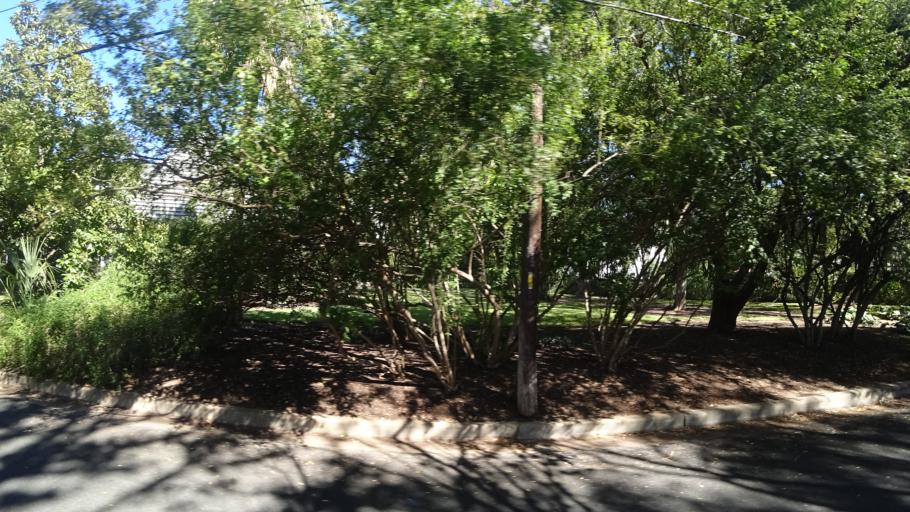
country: US
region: Texas
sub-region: Travis County
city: Rollingwood
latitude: 30.2888
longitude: -97.7657
